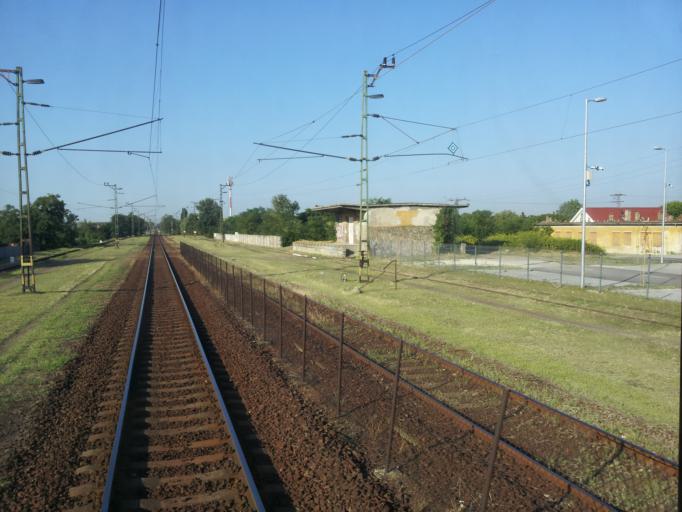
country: HU
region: Pest
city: Dunaharaszti
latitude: 47.3515
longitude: 19.0959
